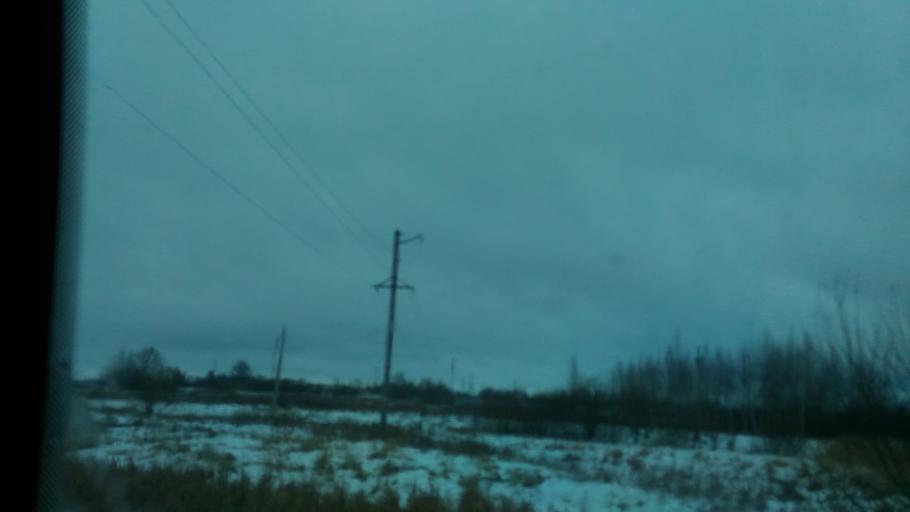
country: RU
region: Tula
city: Bolokhovo
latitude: 54.0604
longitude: 37.8037
